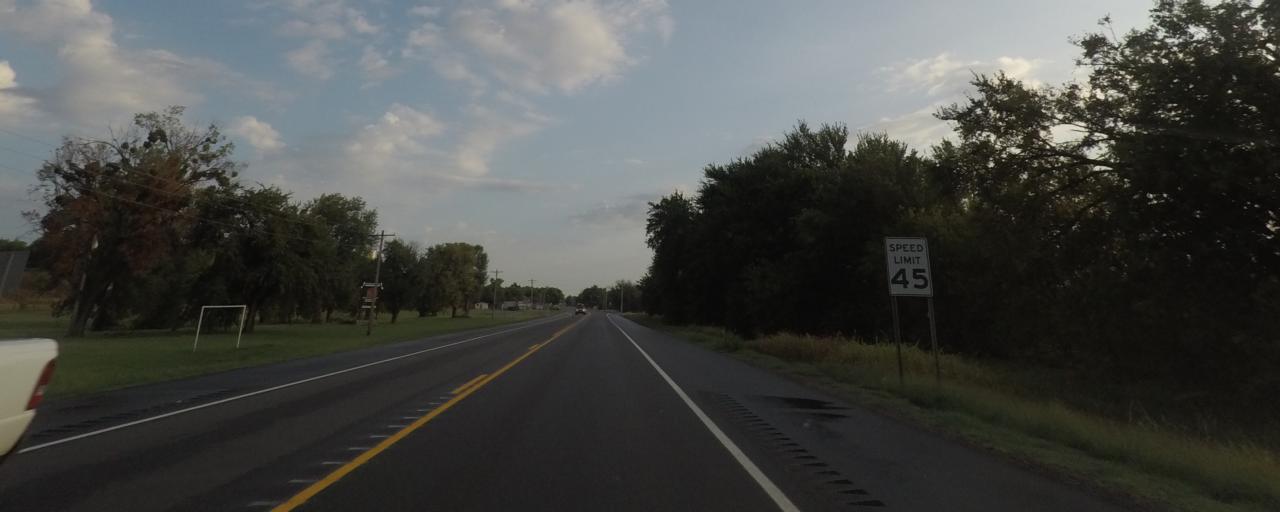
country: US
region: Oklahoma
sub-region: Stephens County
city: Comanche
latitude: 34.3596
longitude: -97.9645
